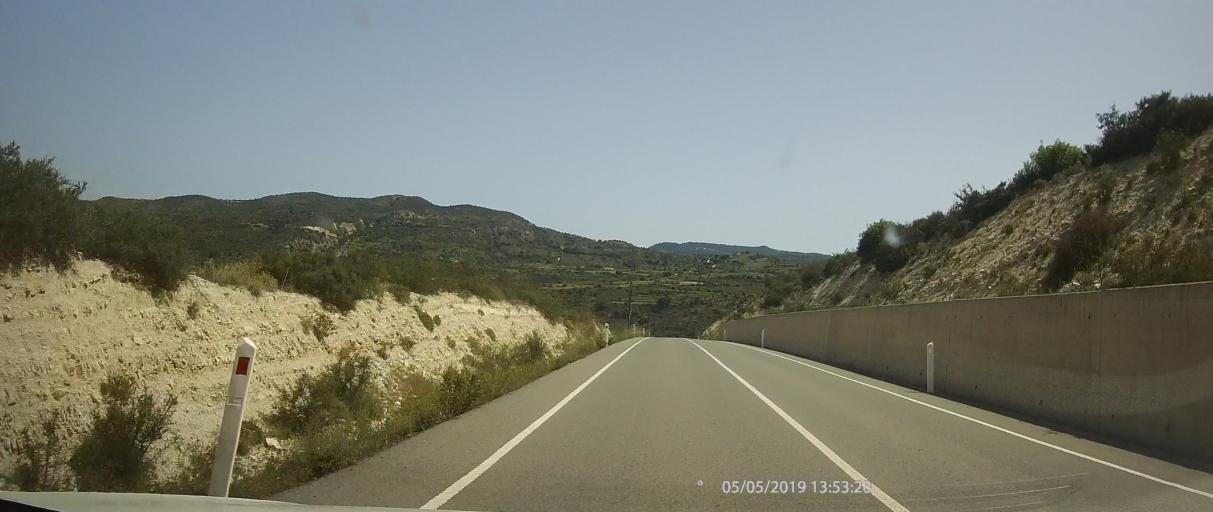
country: CY
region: Limassol
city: Pachna
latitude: 34.8202
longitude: 32.7247
